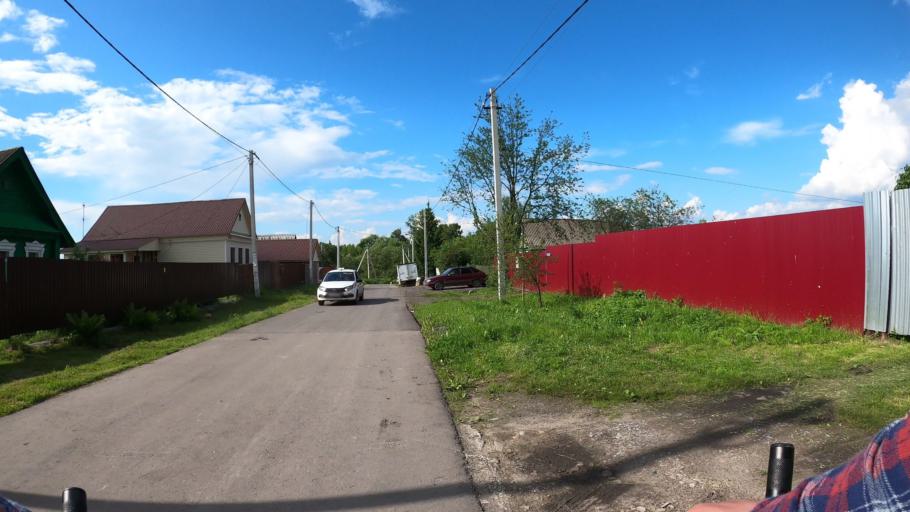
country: RU
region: Moskovskaya
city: Konobeyevo
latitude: 55.4213
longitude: 38.6500
